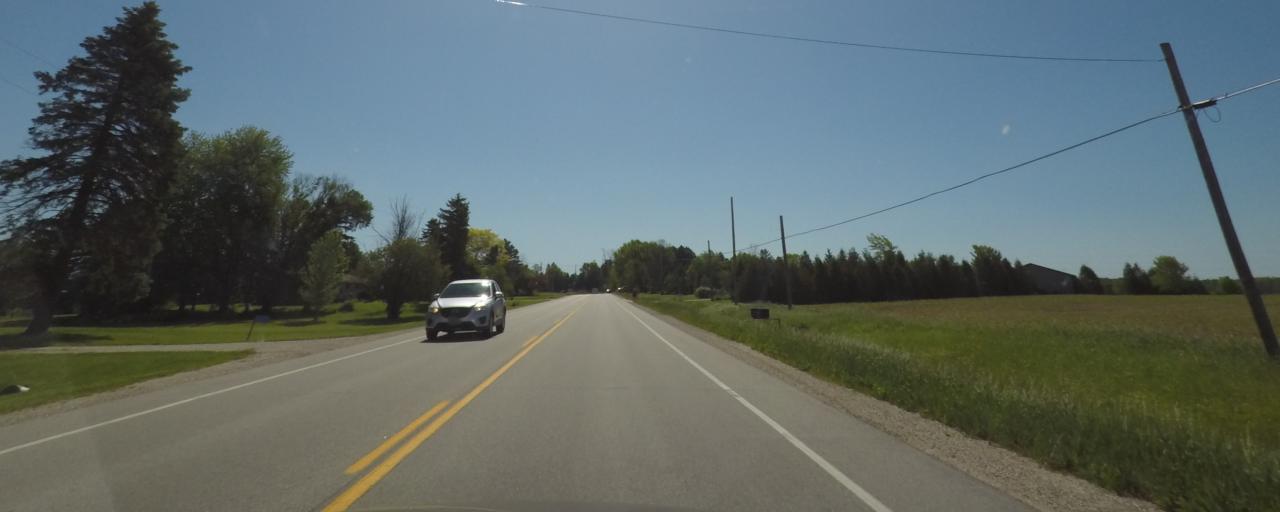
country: US
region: Wisconsin
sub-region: Sheboygan County
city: Sheboygan Falls
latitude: 43.7430
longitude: -87.8724
